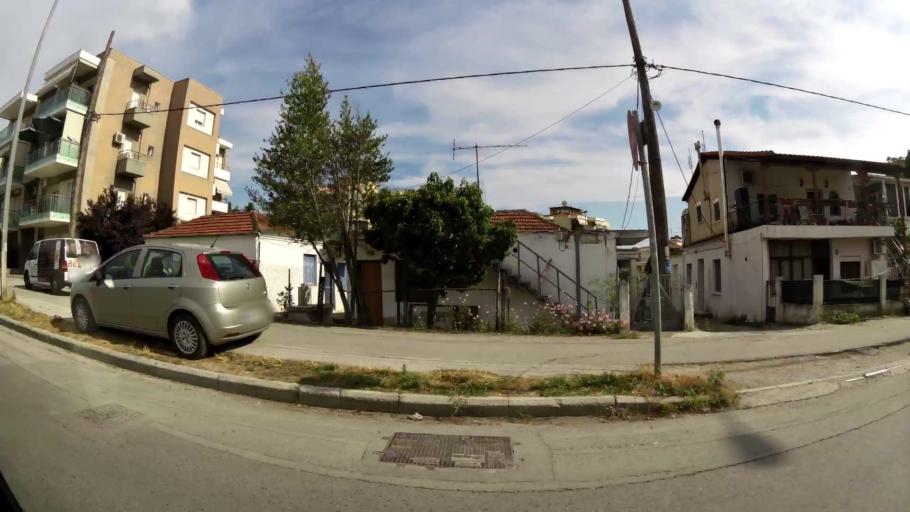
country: GR
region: Central Macedonia
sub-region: Nomos Thessalonikis
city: Kalamaria
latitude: 40.5784
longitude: 22.9606
